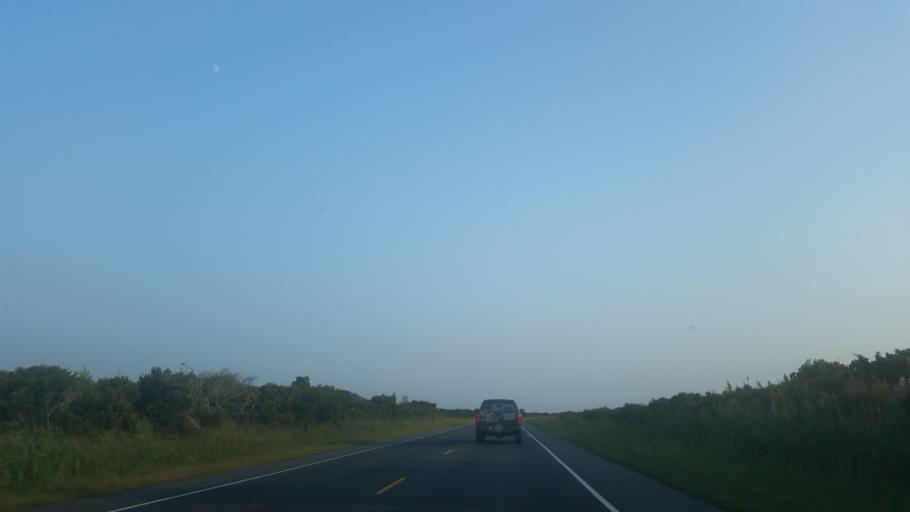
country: US
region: North Carolina
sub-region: Dare County
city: Wanchese
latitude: 35.6419
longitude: -75.4739
